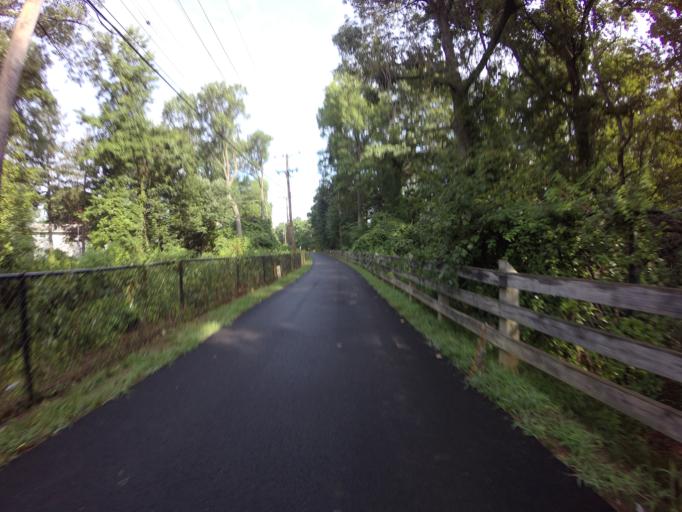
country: US
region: Maryland
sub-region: Anne Arundel County
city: South Gate
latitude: 39.1426
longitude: -76.6083
